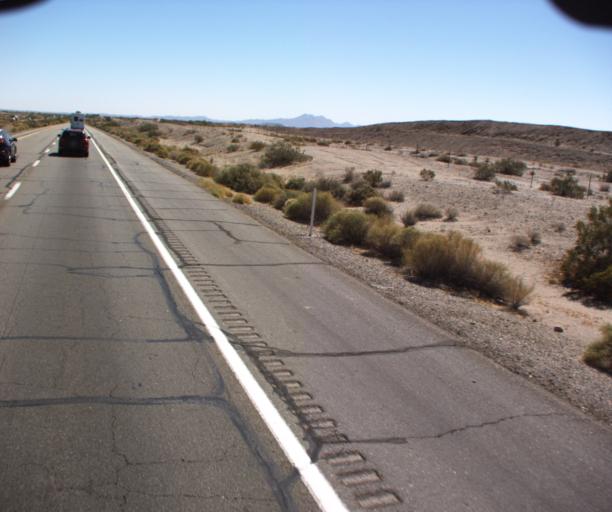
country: US
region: Arizona
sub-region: Yuma County
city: Wellton
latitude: 32.6539
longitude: -114.2309
